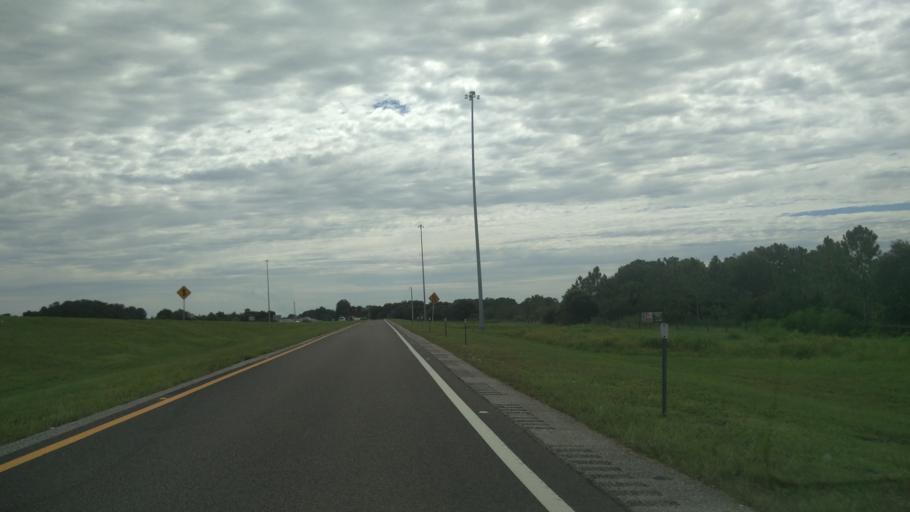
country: US
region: Florida
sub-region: Sarasota County
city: Plantation
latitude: 27.1098
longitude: -82.3824
